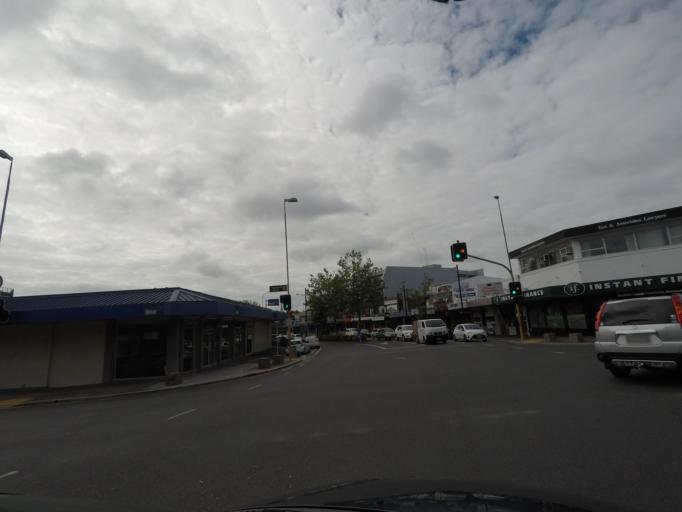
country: NZ
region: Auckland
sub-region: Auckland
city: Rosebank
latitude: -36.8794
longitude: 174.6319
